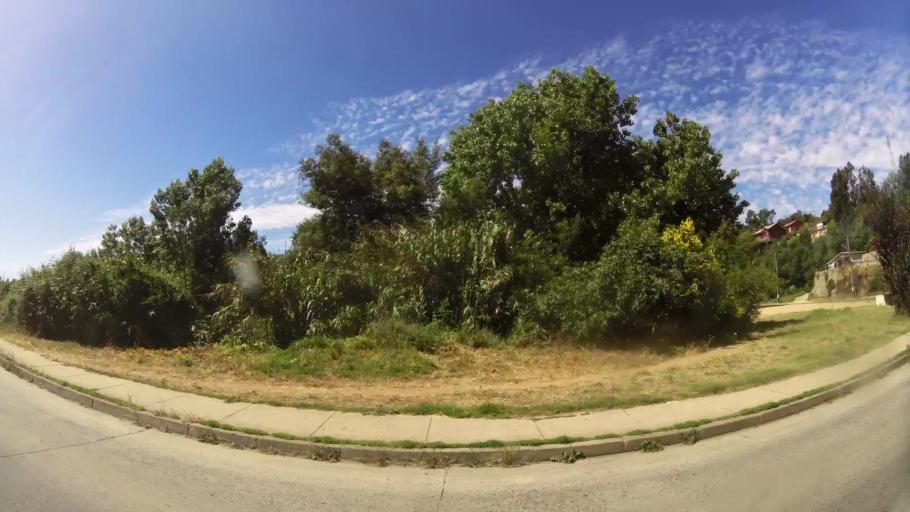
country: CL
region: Valparaiso
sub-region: Provincia de Valparaiso
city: Vina del Mar
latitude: -33.0439
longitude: -71.5720
